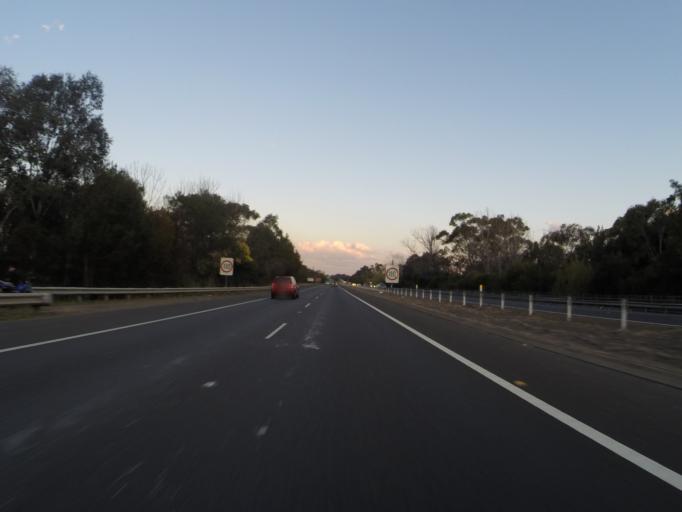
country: AU
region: New South Wales
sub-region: Penrith Municipality
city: Glenmore Park
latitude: -33.7659
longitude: 150.6617
